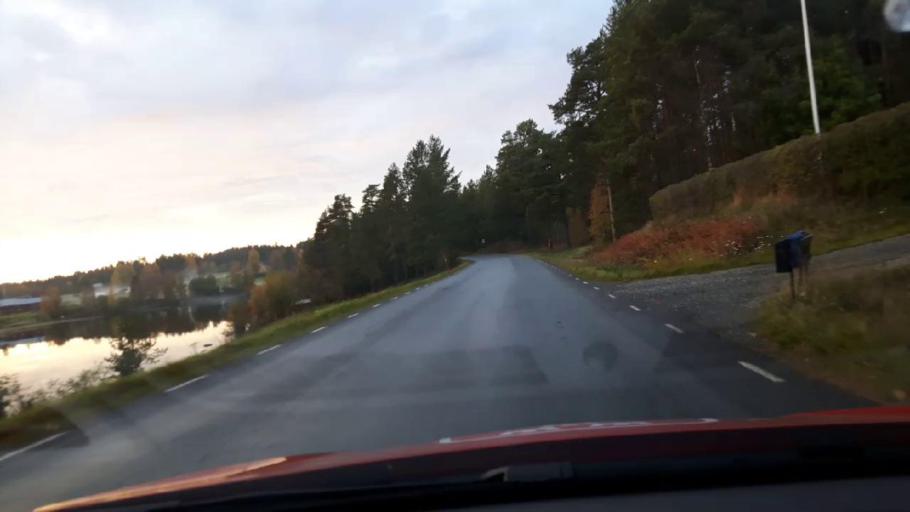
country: SE
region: Jaemtland
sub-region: OEstersunds Kommun
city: Lit
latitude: 63.3214
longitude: 14.9135
